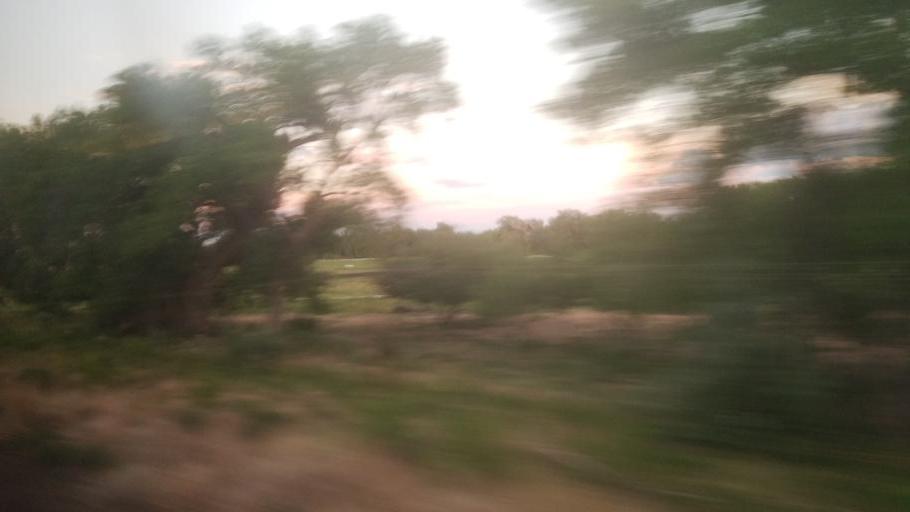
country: US
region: Colorado
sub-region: Las Animas County
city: Trinidad
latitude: 37.2438
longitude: -104.4217
